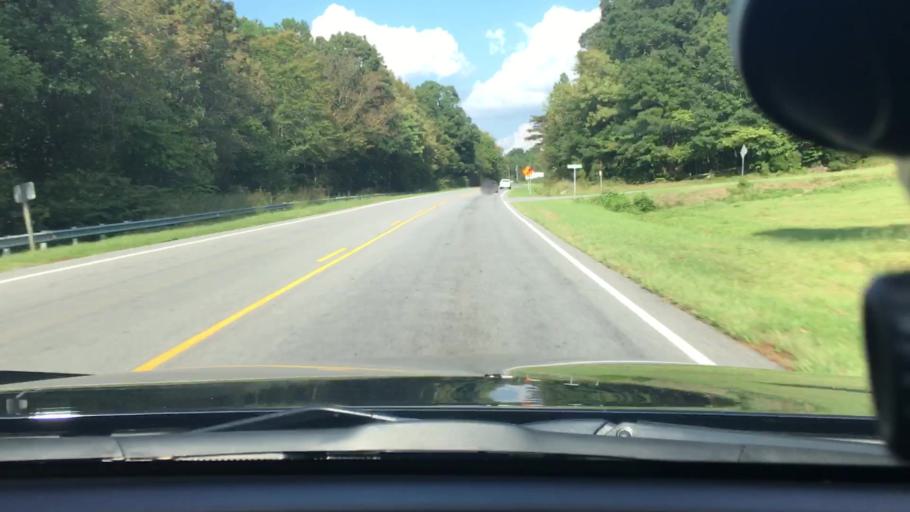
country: US
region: North Carolina
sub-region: Randolph County
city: Asheboro
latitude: 35.6714
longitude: -79.8733
